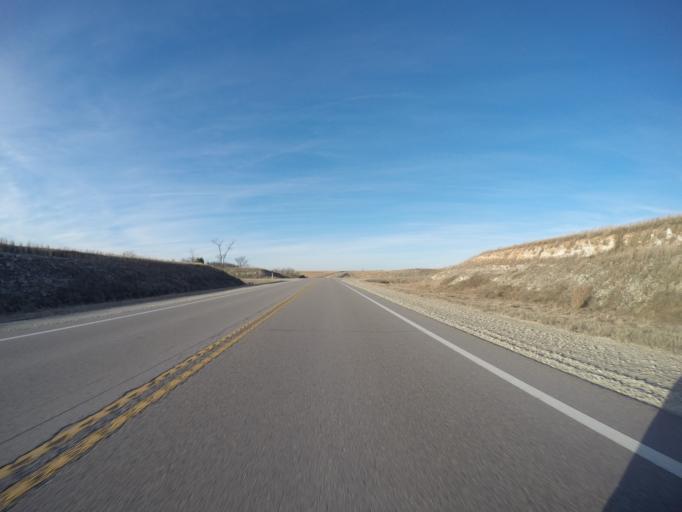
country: US
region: Kansas
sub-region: Marion County
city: Marion
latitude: 38.2894
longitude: -96.9651
